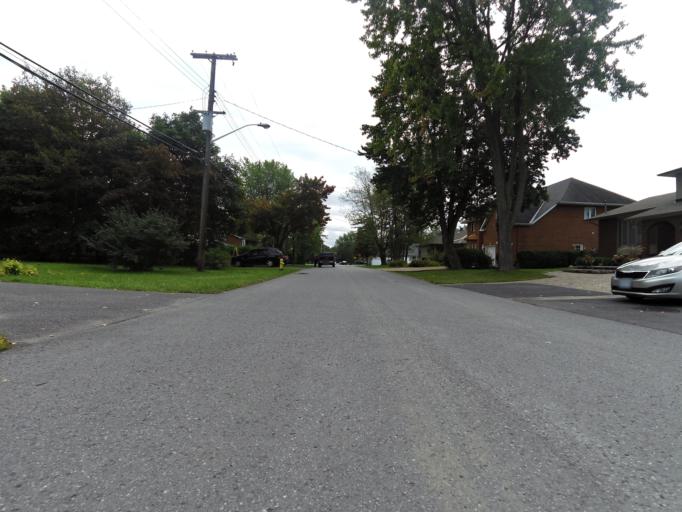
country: CA
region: Ontario
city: Ottawa
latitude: 45.3575
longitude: -75.7061
